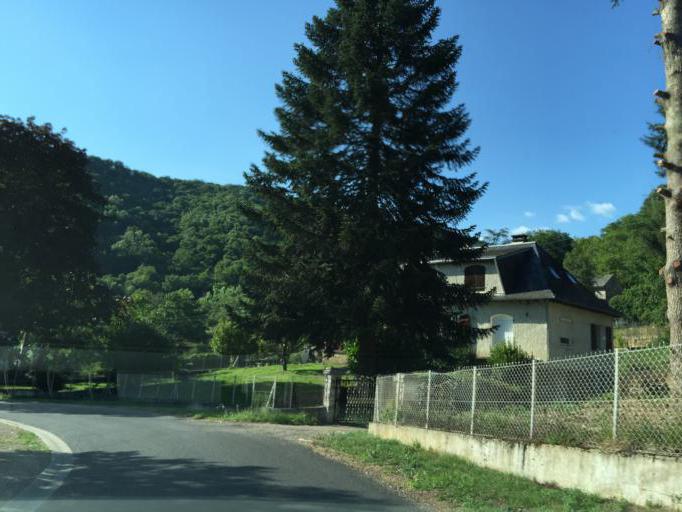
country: FR
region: Midi-Pyrenees
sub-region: Departement de l'Aveyron
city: Espalion
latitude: 44.5653
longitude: 2.6820
